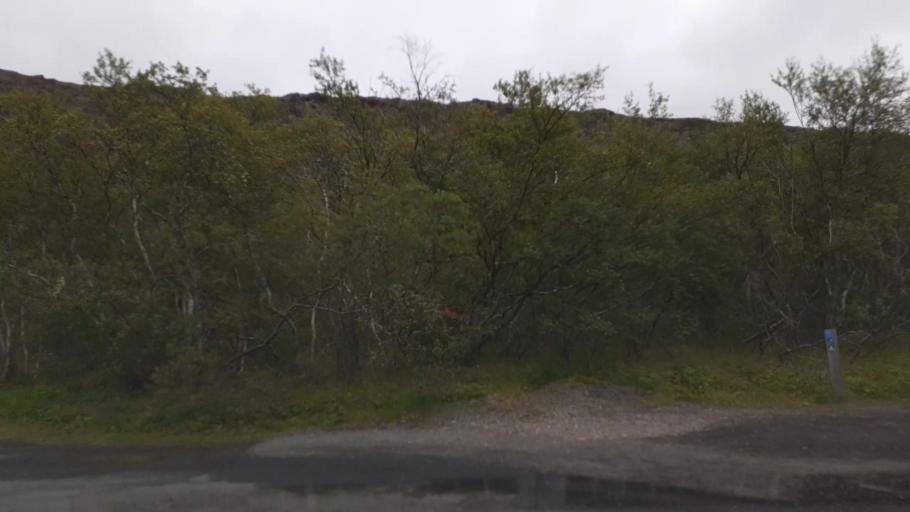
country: IS
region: Northeast
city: Husavik
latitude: 66.0016
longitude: -16.5127
